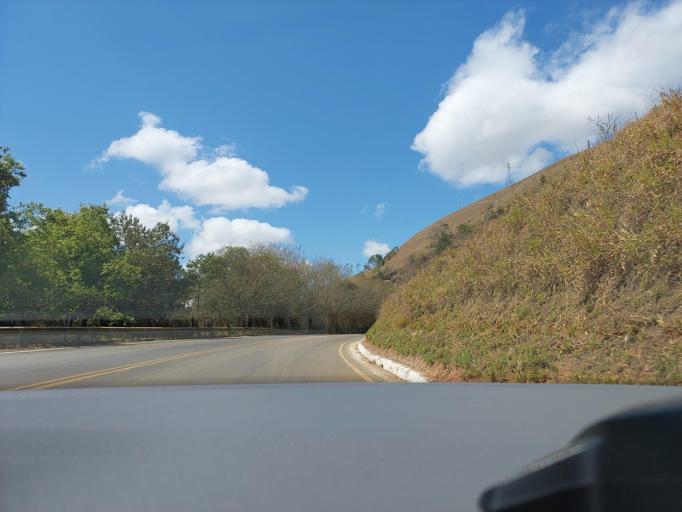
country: BR
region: Minas Gerais
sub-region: Muriae
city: Muriae
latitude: -21.0745
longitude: -42.5040
